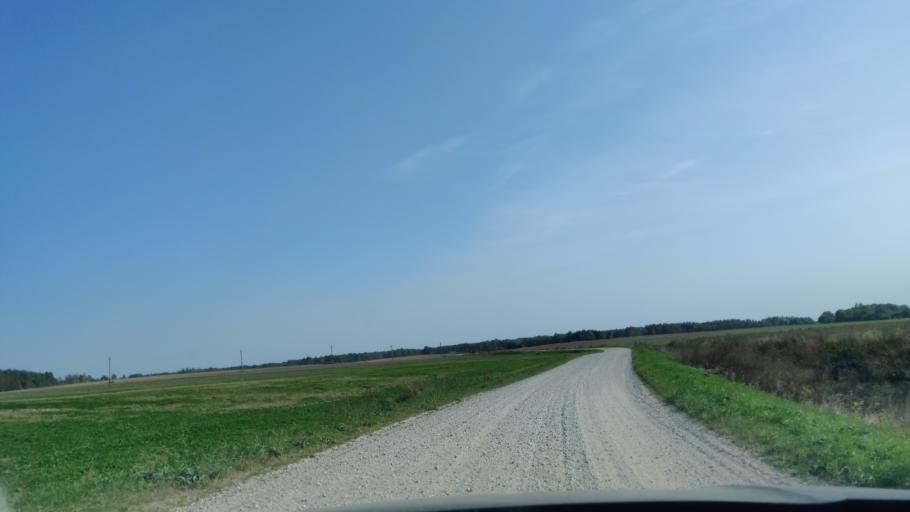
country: LT
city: Sirvintos
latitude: 54.9695
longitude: 24.8411
